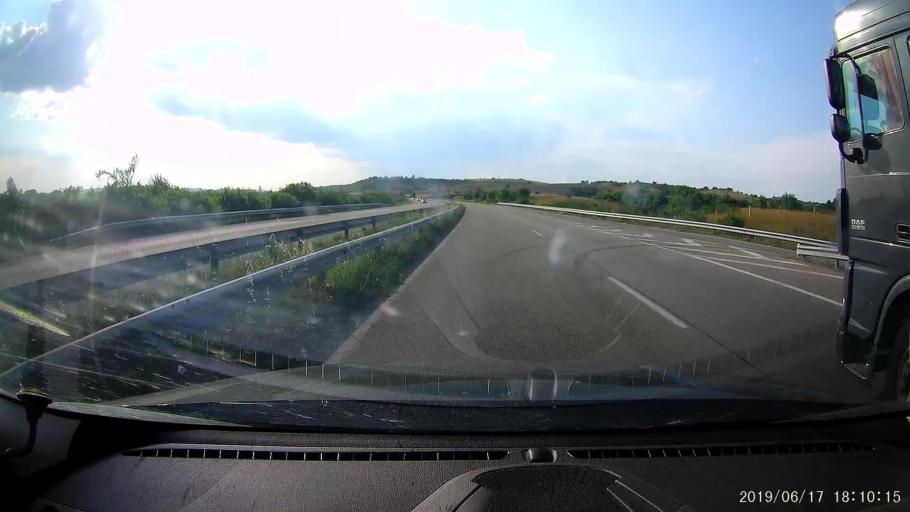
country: BG
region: Khaskovo
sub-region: Obshtina Lyubimets
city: Lyubimets
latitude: 41.8724
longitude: 26.0809
